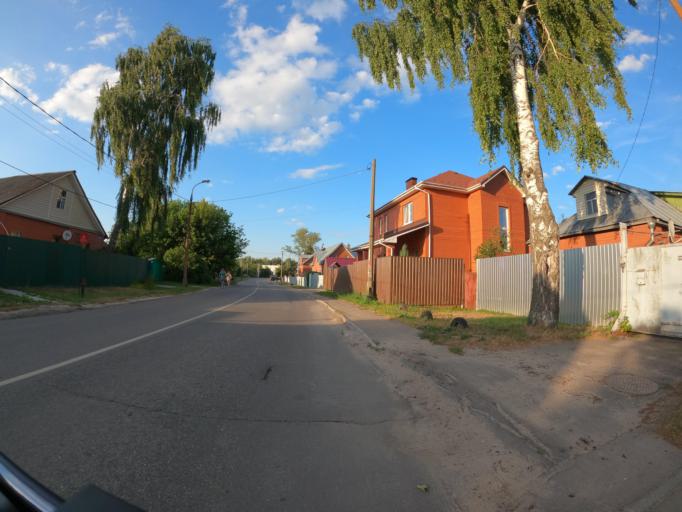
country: RU
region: Moskovskaya
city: Raduzhnyy
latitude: 55.1060
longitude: 38.7393
